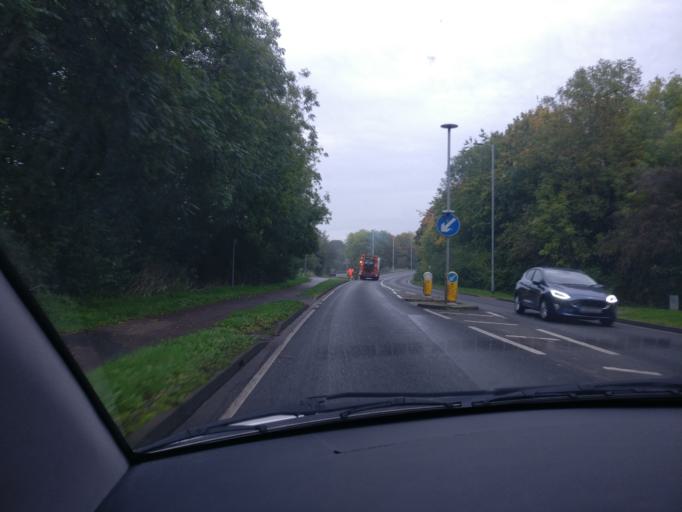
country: GB
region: England
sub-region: Peterborough
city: Castor
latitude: 52.5549
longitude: -0.3047
